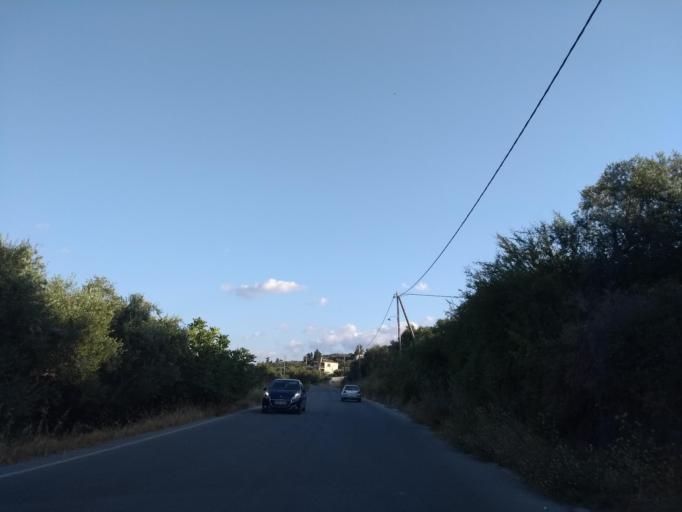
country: GR
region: Crete
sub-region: Nomos Chanias
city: Kalivai
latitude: 35.4414
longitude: 24.1754
